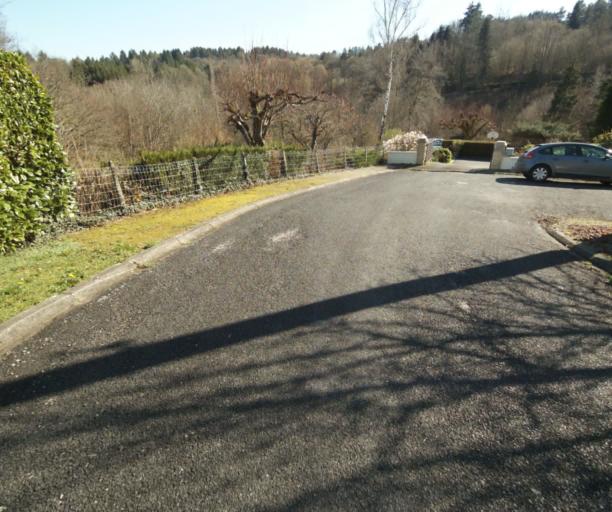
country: FR
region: Limousin
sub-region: Departement de la Correze
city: Tulle
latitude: 45.2896
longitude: 1.7223
